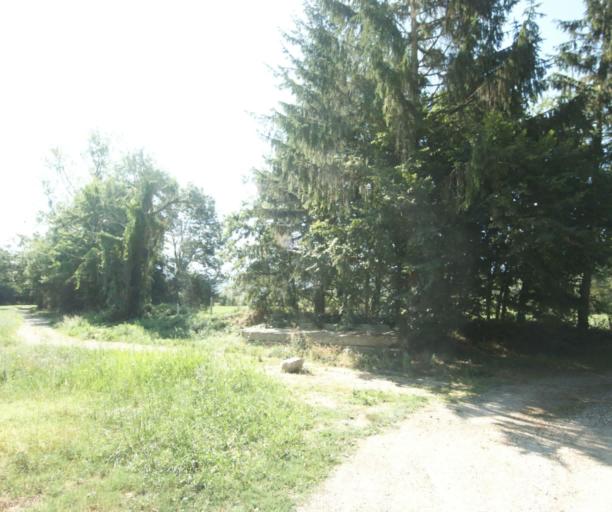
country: FR
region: Midi-Pyrenees
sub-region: Departement du Tarn
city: Soreze
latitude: 43.4577
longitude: 2.0428
